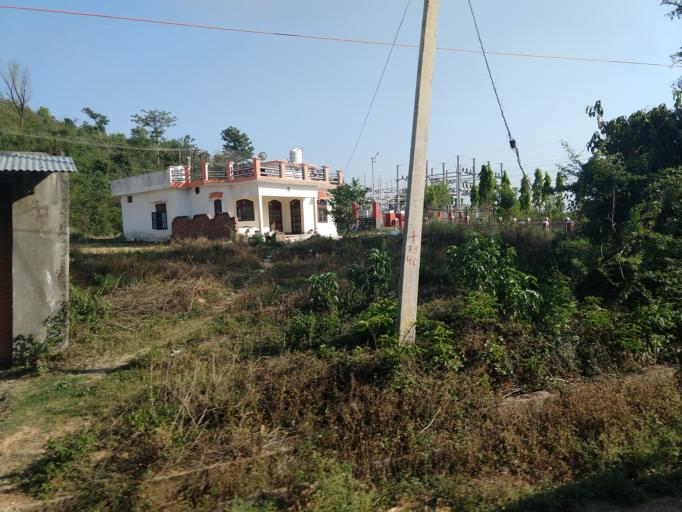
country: IN
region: Himachal Pradesh
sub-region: Chamba
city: Chowari
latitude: 32.3521
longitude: 75.9152
